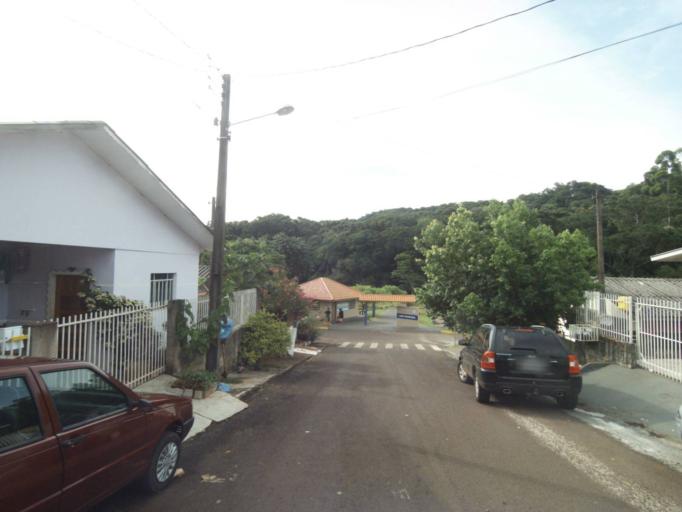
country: BR
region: Parana
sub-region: Guaraniacu
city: Guaraniacu
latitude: -25.1006
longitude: -52.8774
